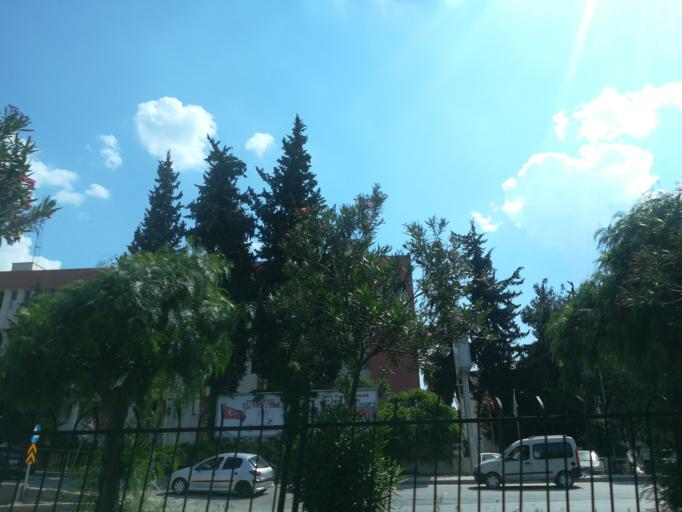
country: TR
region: Adana
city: Adana
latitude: 36.9893
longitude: 35.3422
